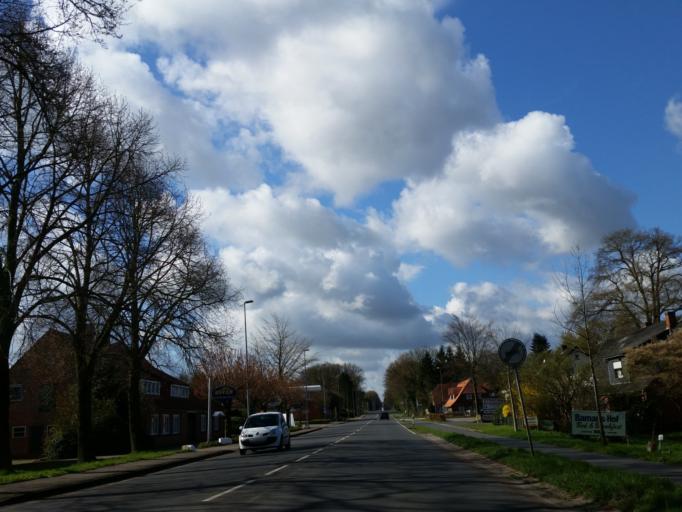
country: DE
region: Lower Saxony
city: Ahausen
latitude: 53.0816
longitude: 9.3584
